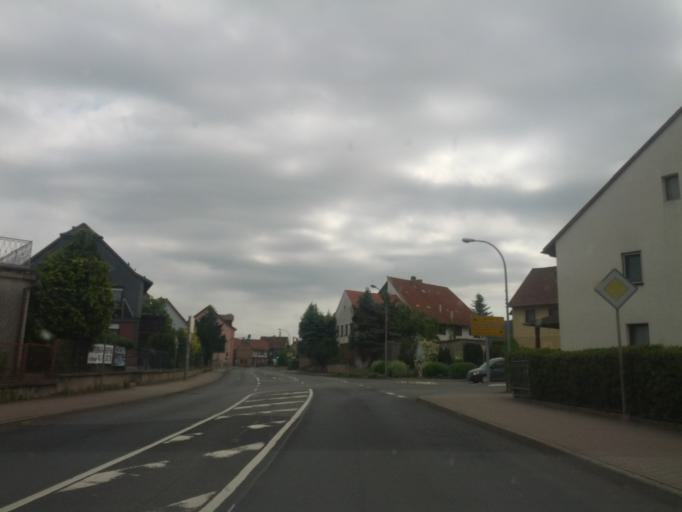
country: DE
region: Thuringia
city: Dorndorf
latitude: 50.8377
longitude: 10.0835
